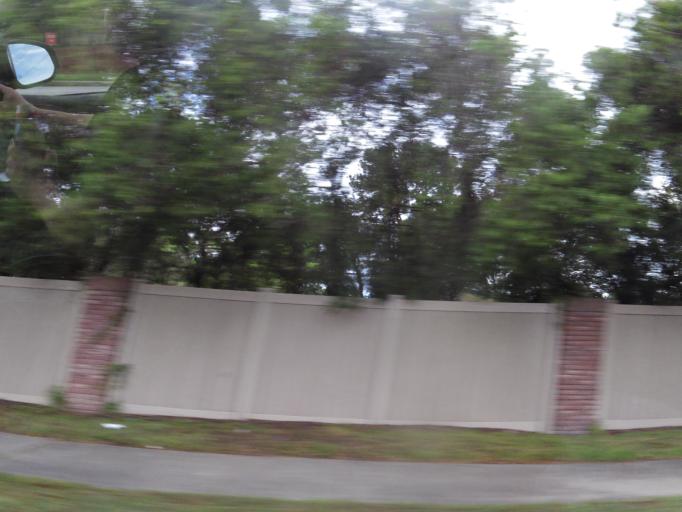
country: US
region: Florida
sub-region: Clay County
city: Lakeside
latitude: 30.1017
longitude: -81.7408
